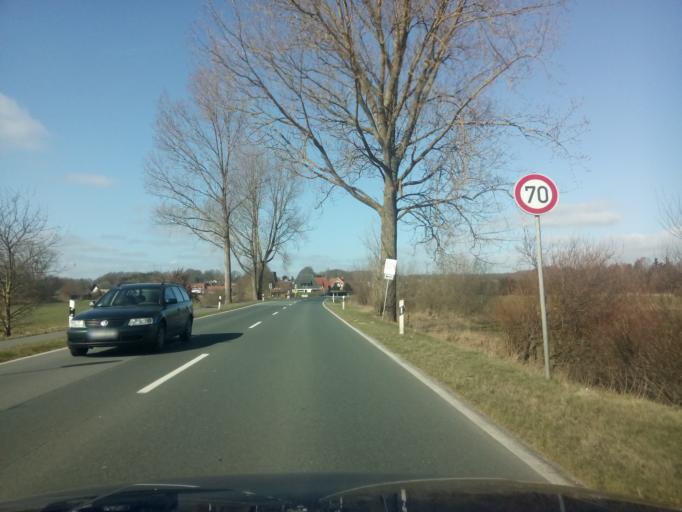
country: DE
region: Lower Saxony
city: Osterholz-Scharmbeck
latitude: 53.2160
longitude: 8.8105
